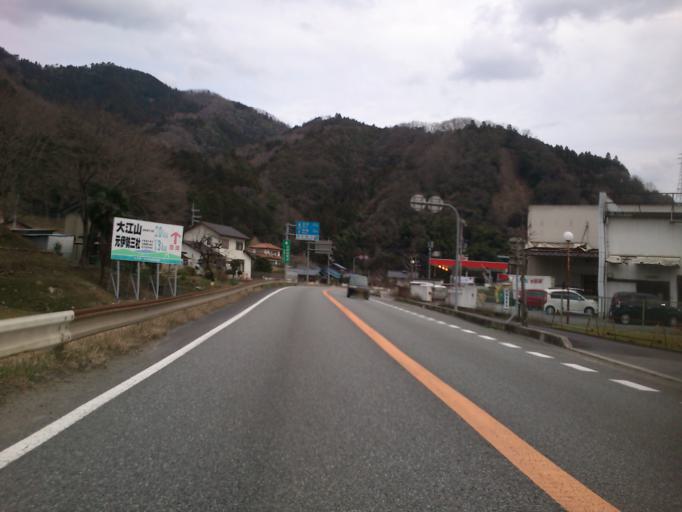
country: JP
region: Kyoto
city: Fukuchiyama
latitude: 35.3369
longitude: 135.0987
